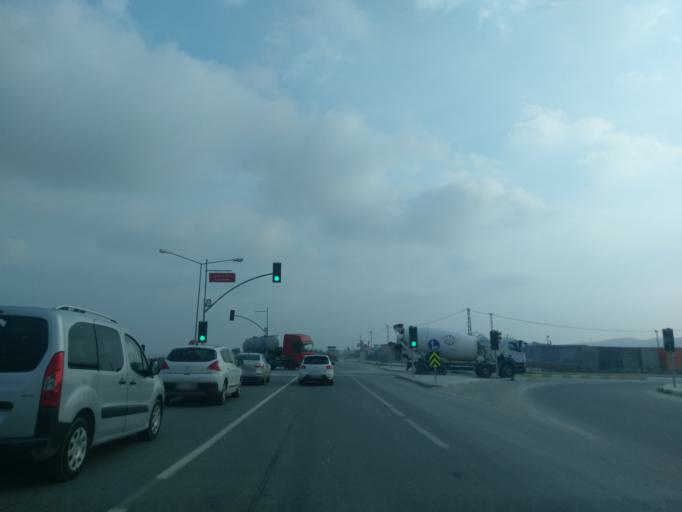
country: TR
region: Istanbul
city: Muratbey
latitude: 41.1075
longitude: 28.5051
